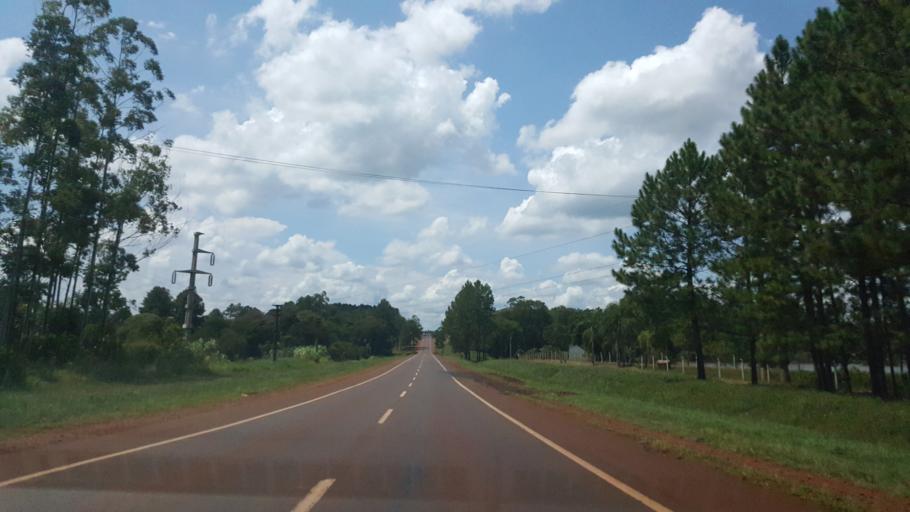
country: AR
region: Misiones
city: Garuhape
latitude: -26.8171
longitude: -54.9490
